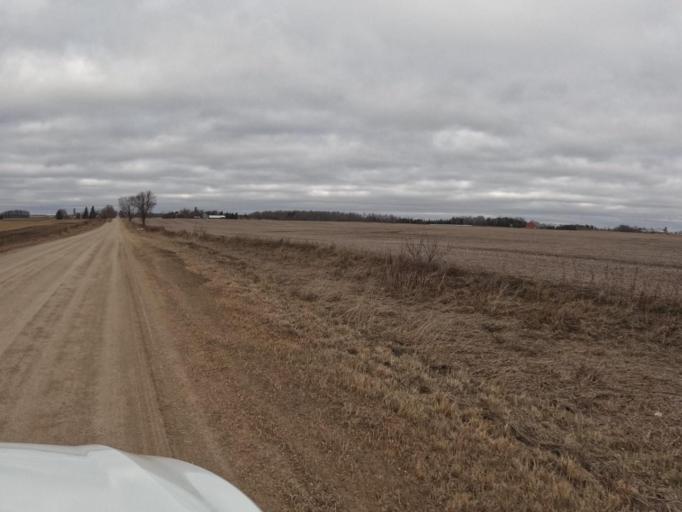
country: CA
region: Ontario
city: Shelburne
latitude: 43.8727
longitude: -80.4024
